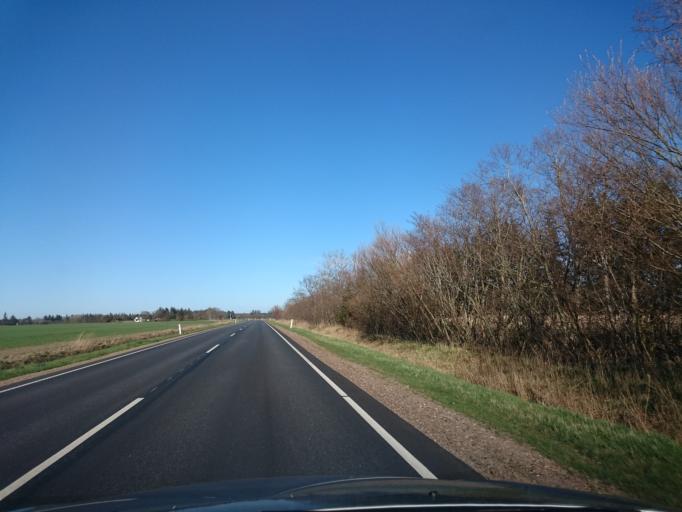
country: DK
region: North Denmark
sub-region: Hjorring Kommune
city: Sindal
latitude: 57.5963
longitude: 10.3065
